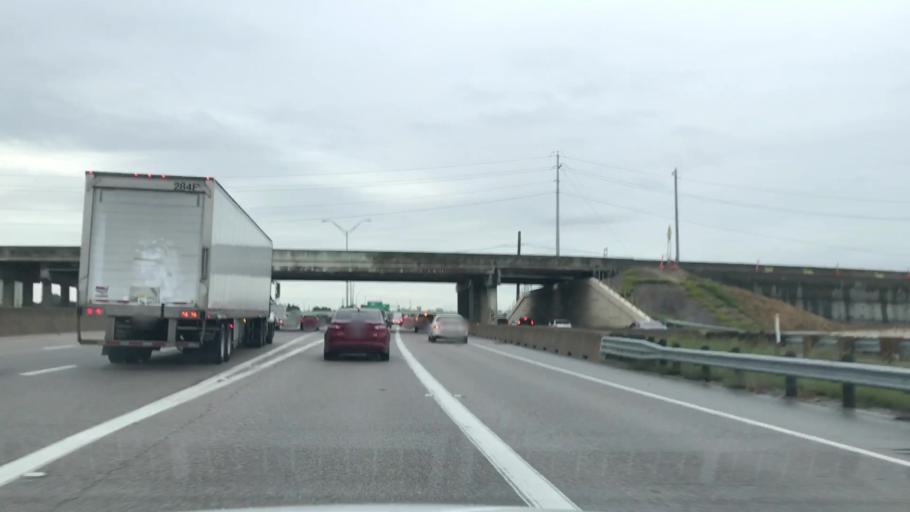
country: US
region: Texas
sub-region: Dallas County
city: Coppell
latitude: 32.9545
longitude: -97.0399
